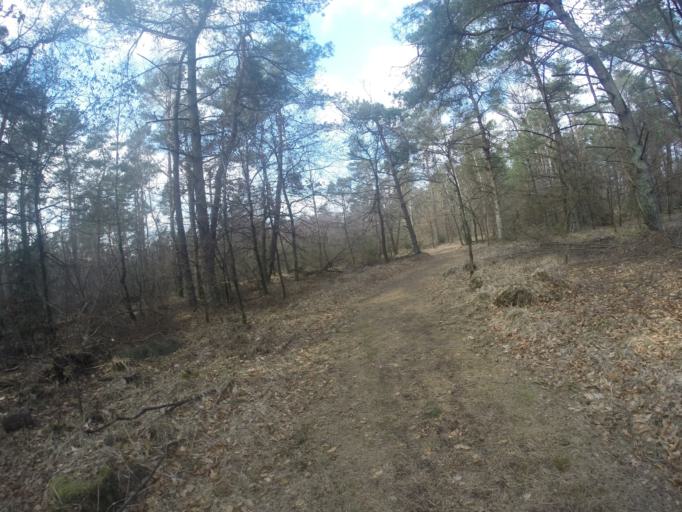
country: NL
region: Gelderland
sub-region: Gemeente Lochem
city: Almen
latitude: 52.1297
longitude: 6.3235
